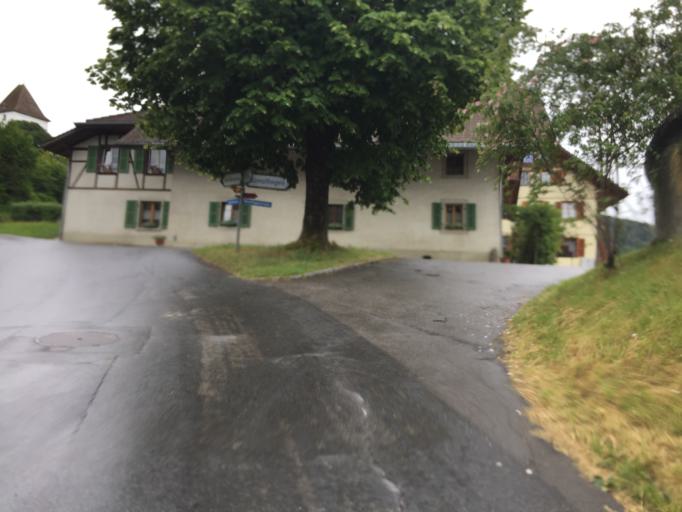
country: CH
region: Bern
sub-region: Bern-Mittelland District
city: Biglen
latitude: 46.9092
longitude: 7.6058
